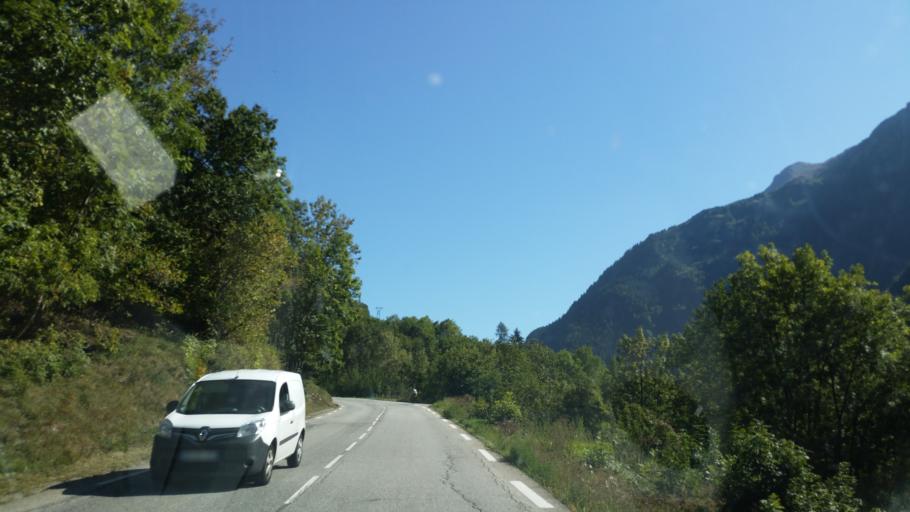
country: FR
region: Rhone-Alpes
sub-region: Departement de la Savoie
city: Tignes
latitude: 45.5771
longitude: 6.8830
